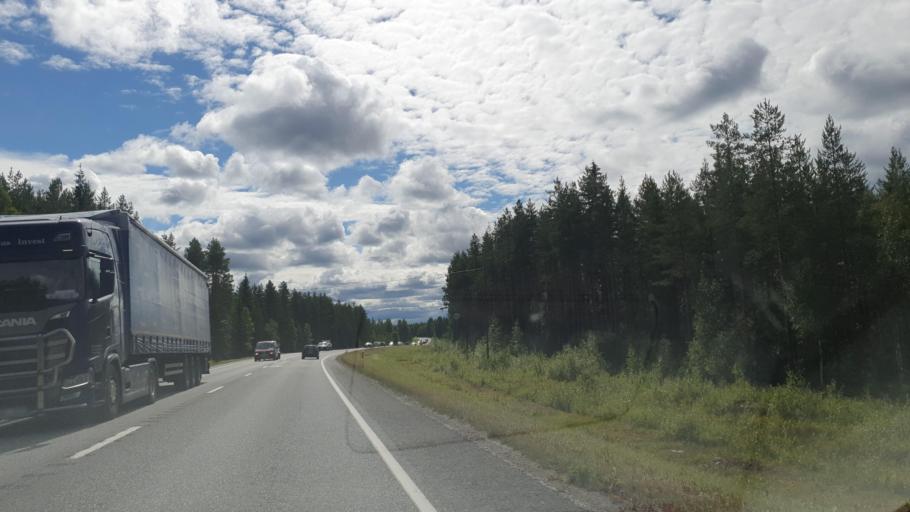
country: FI
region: Kainuu
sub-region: Kajaani
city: Kajaani
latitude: 64.1512
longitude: 27.5114
